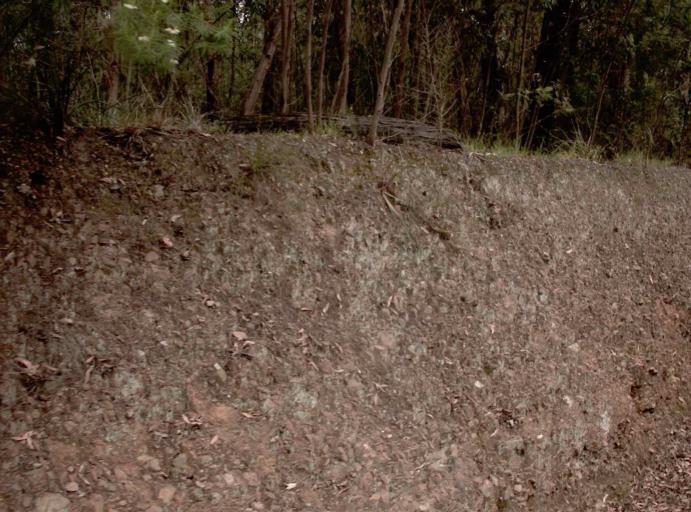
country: AU
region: Victoria
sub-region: Wellington
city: Heyfield
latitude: -37.7528
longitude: 146.6691
